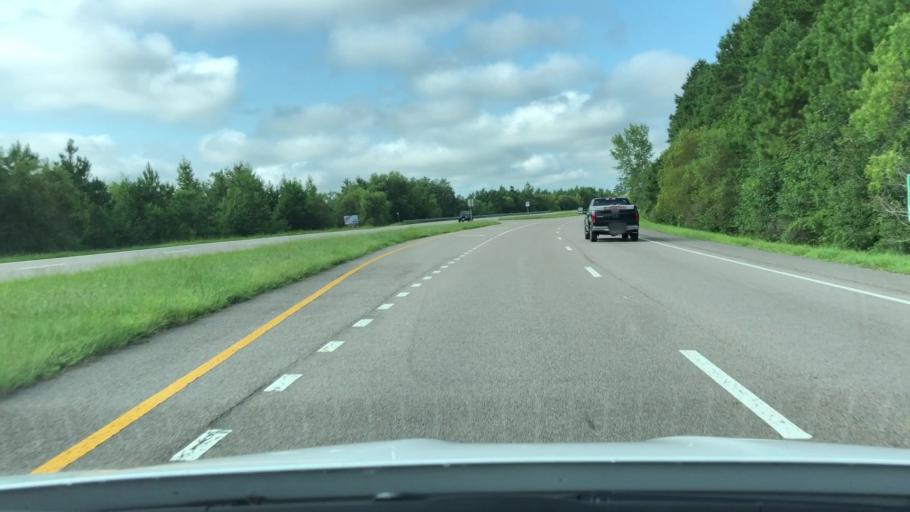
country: US
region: Virginia
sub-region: City of Portsmouth
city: Portsmouth Heights
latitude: 36.6766
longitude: -76.3478
